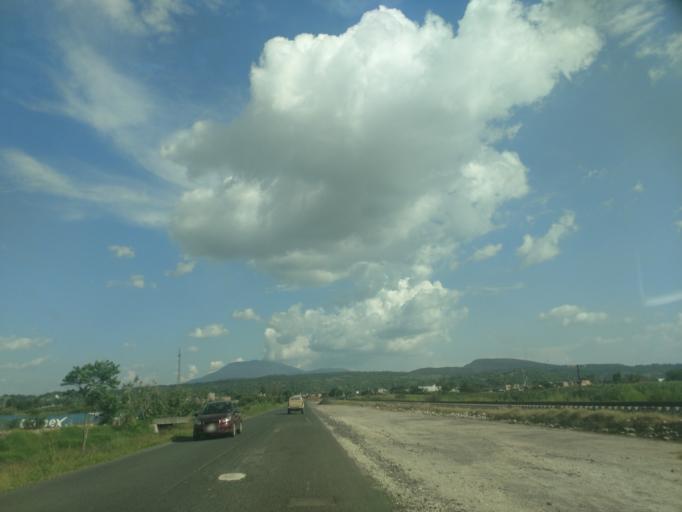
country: MX
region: Jalisco
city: Antonio Escobedo
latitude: 20.9089
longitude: -103.9886
